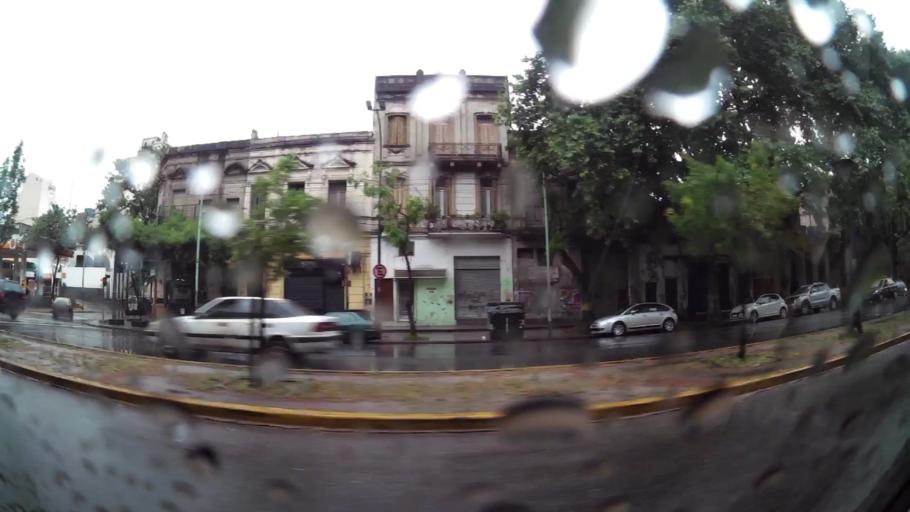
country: AR
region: Buenos Aires F.D.
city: Buenos Aires
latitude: -34.6304
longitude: -58.3630
